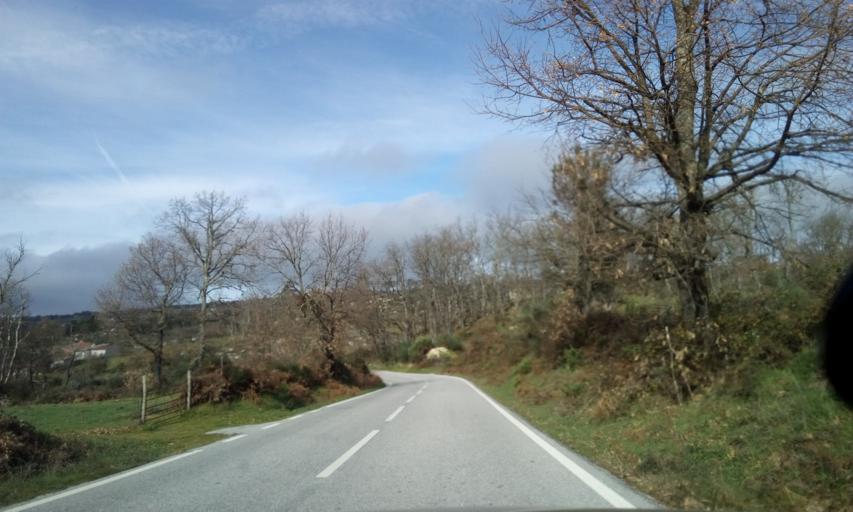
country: PT
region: Guarda
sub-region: Aguiar da Beira
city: Aguiar da Beira
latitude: 40.7471
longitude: -7.5515
